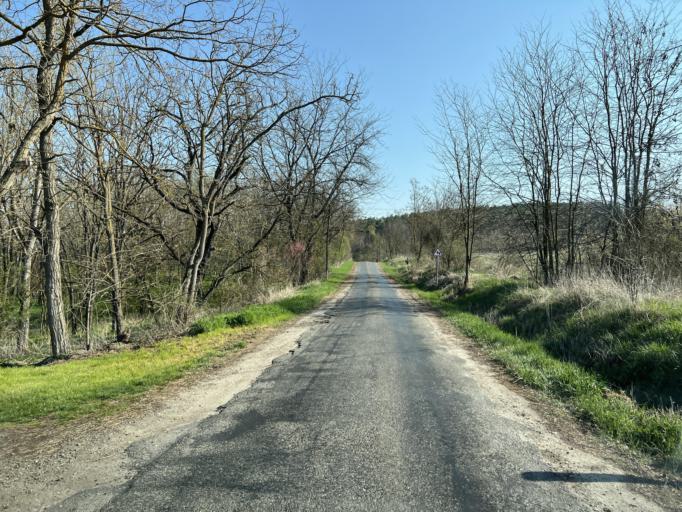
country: SK
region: Nitriansky
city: Sahy
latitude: 47.9931
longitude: 18.8171
